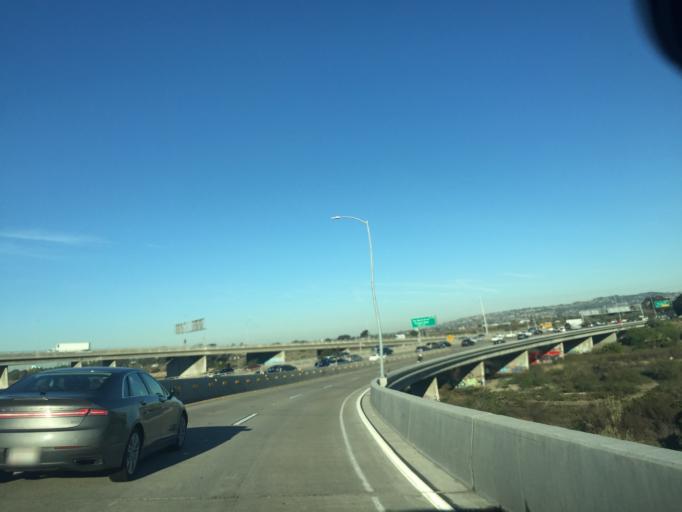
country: US
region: California
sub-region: San Diego County
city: San Diego
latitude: 32.7601
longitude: -117.2031
